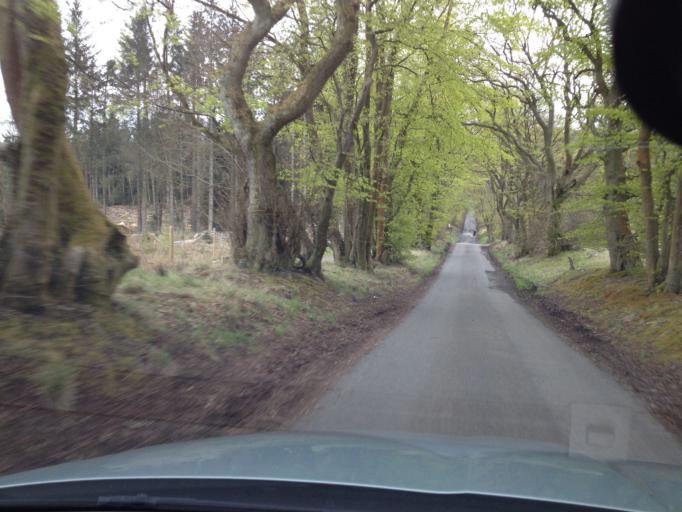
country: GB
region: Scotland
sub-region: West Lothian
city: Linlithgow
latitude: 55.9464
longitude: -3.6046
